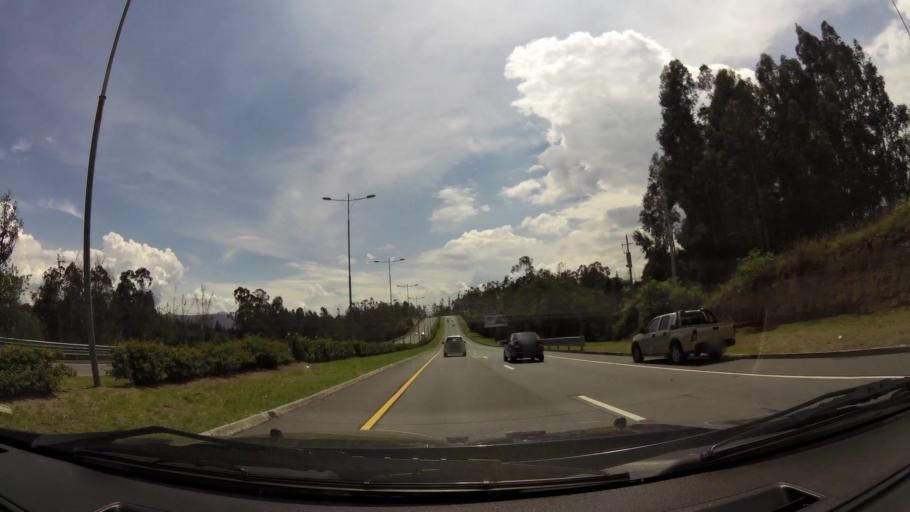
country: EC
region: Pichincha
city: Quito
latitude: -0.1736
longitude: -78.3430
